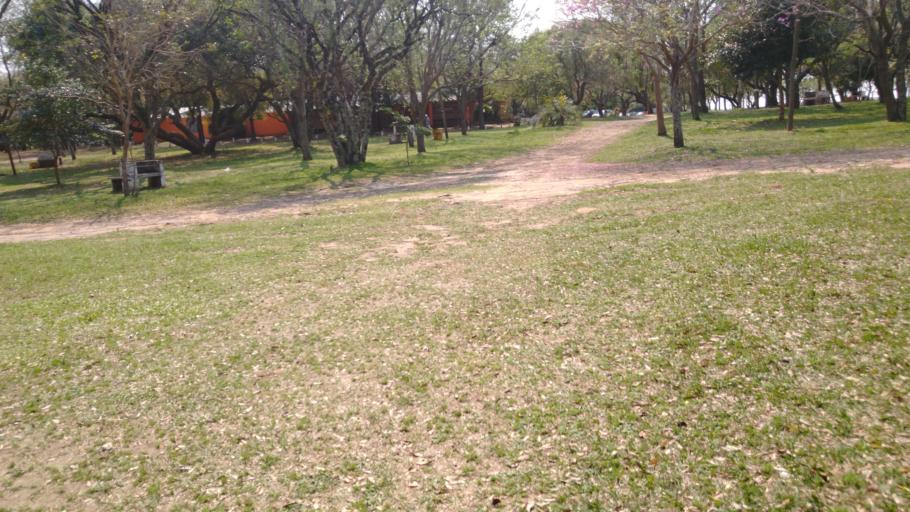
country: AR
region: Corrientes
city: Ituzaingo
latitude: -27.5478
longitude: -56.6748
